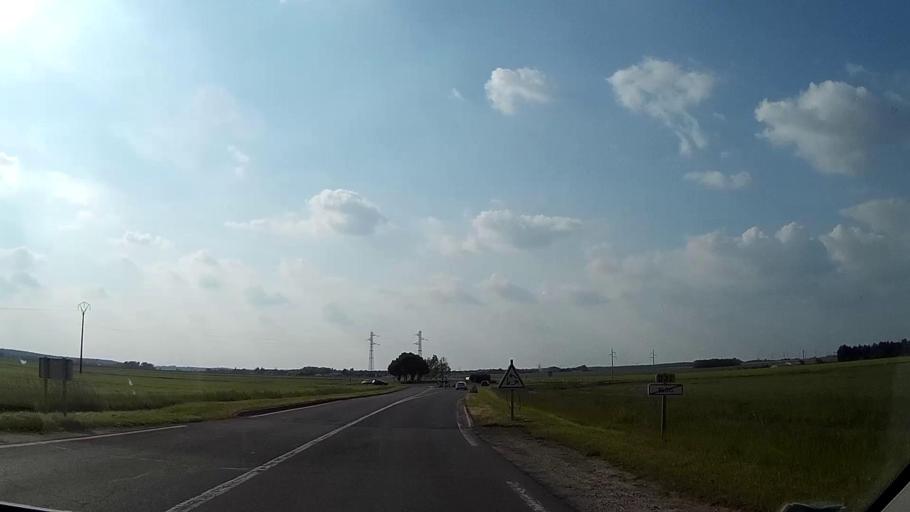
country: FR
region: Centre
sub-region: Departement du Loir-et-Cher
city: Saint-Sulpice-de-Pommeray
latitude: 47.6007
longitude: 1.2946
